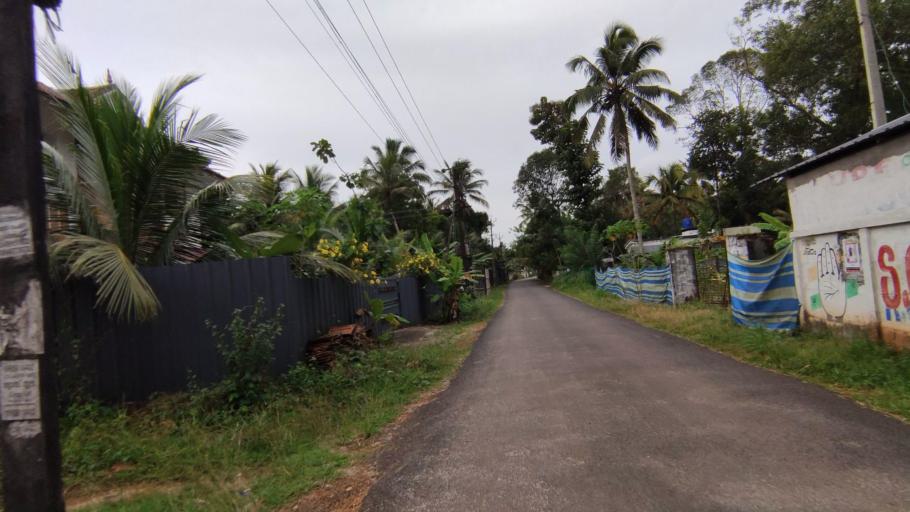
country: IN
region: Kerala
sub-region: Alappuzha
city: Shertallai
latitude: 9.6253
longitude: 76.3565
